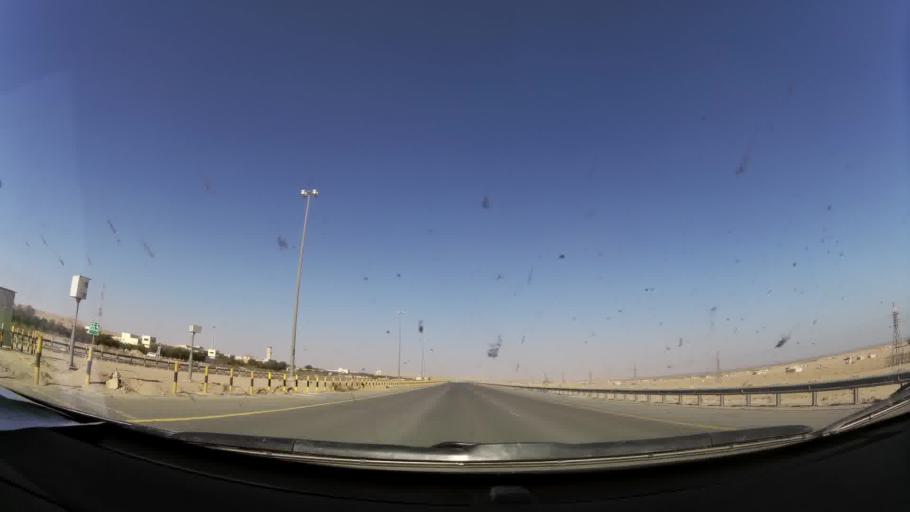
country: KW
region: Muhafazat al Jahra'
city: Al Jahra'
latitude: 29.4584
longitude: 47.7607
